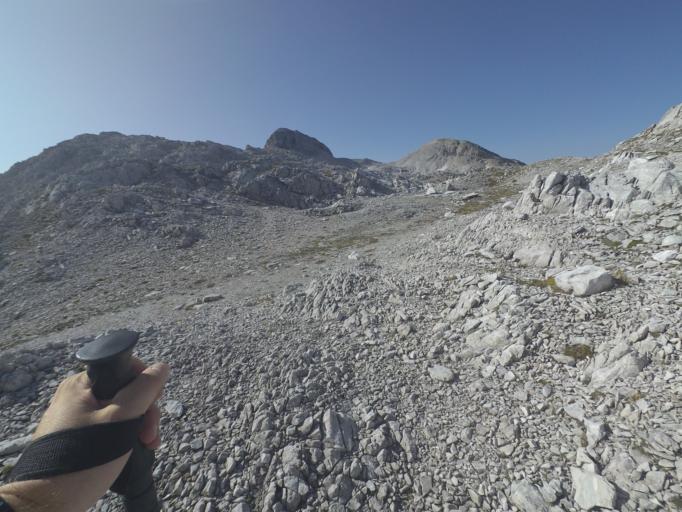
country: AT
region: Salzburg
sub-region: Politischer Bezirk Sankt Johann im Pongau
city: Kleinarl
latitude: 47.2149
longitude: 13.4015
